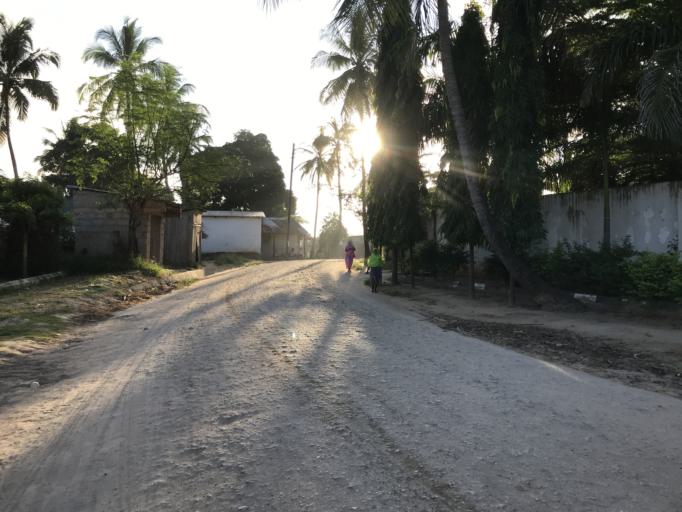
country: TZ
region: Dar es Salaam
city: Dar es Salaam
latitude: -6.8635
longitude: 39.3576
